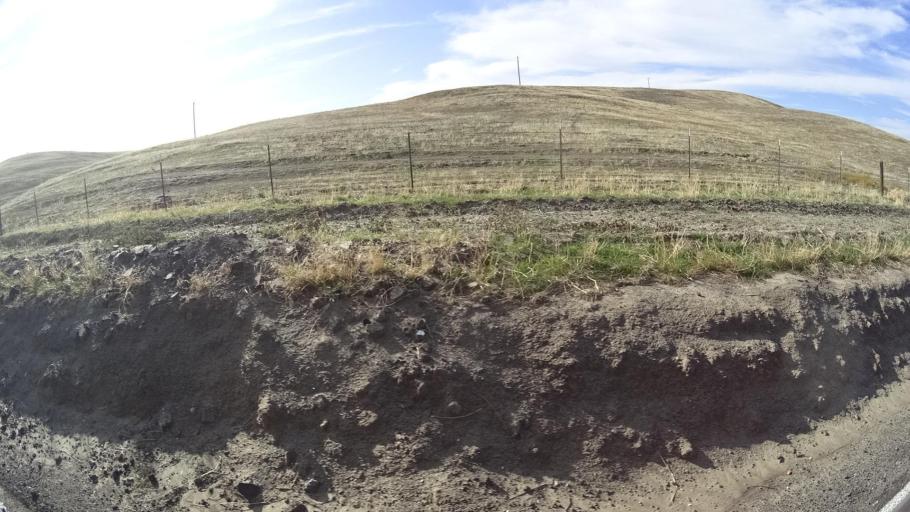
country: US
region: California
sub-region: Kern County
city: Oildale
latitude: 35.6100
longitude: -118.9154
